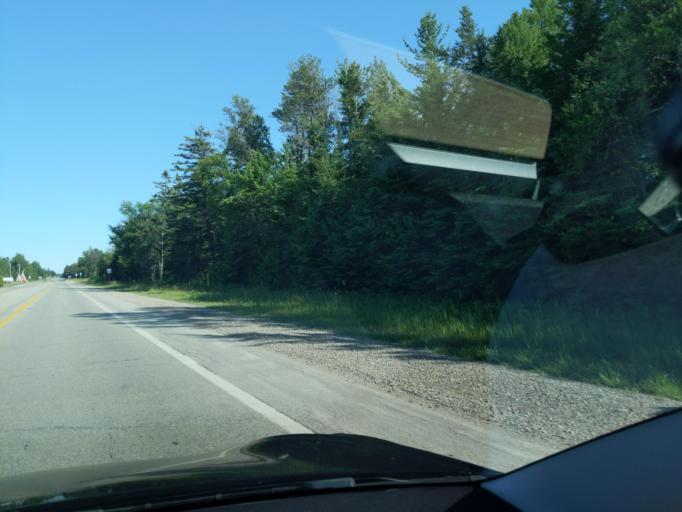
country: US
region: Michigan
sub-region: Mackinac County
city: Saint Ignace
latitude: 45.7652
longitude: -84.7201
